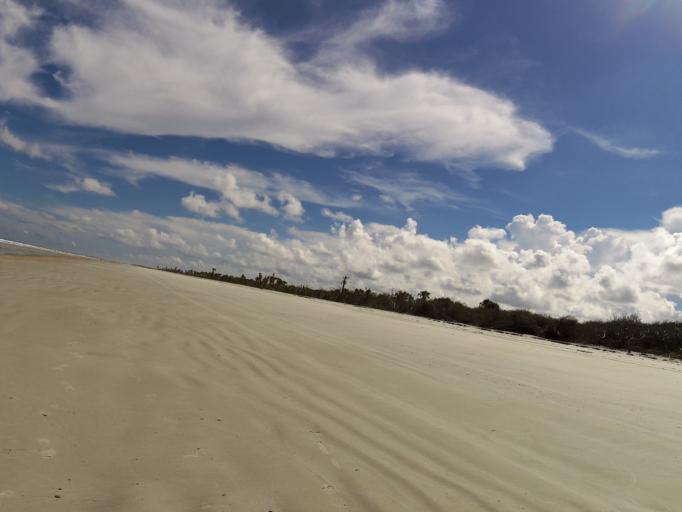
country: US
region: Florida
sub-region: Duval County
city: Atlantic Beach
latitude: 30.4708
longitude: -81.4124
